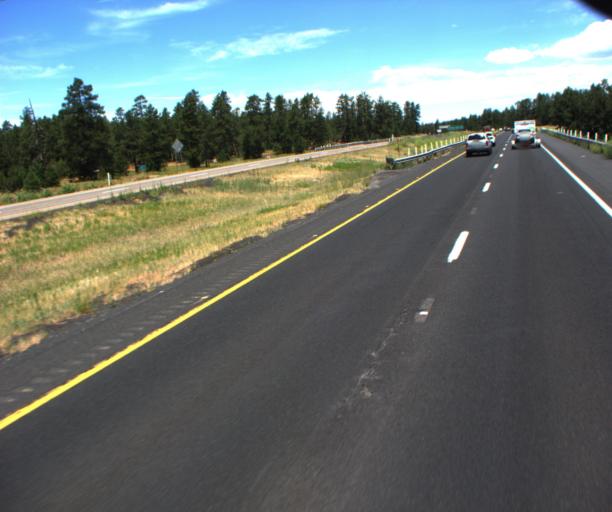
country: US
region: Arizona
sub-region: Coconino County
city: Sedona
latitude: 34.8520
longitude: -111.6064
